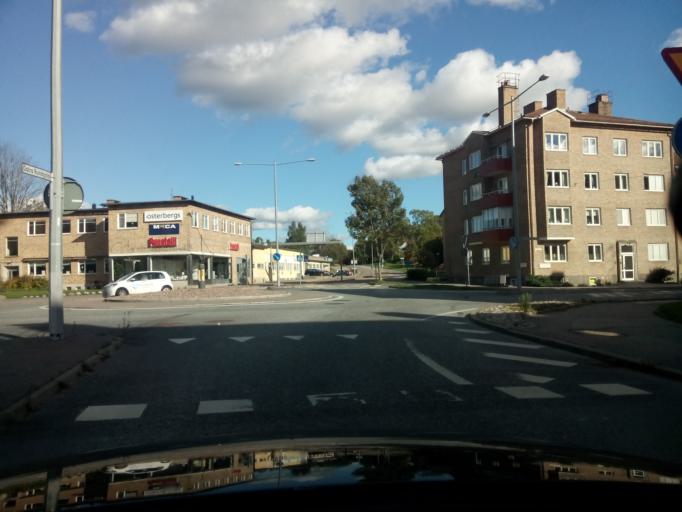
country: SE
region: Soedermanland
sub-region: Nykopings Kommun
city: Nykoping
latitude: 58.7571
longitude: 17.0162
